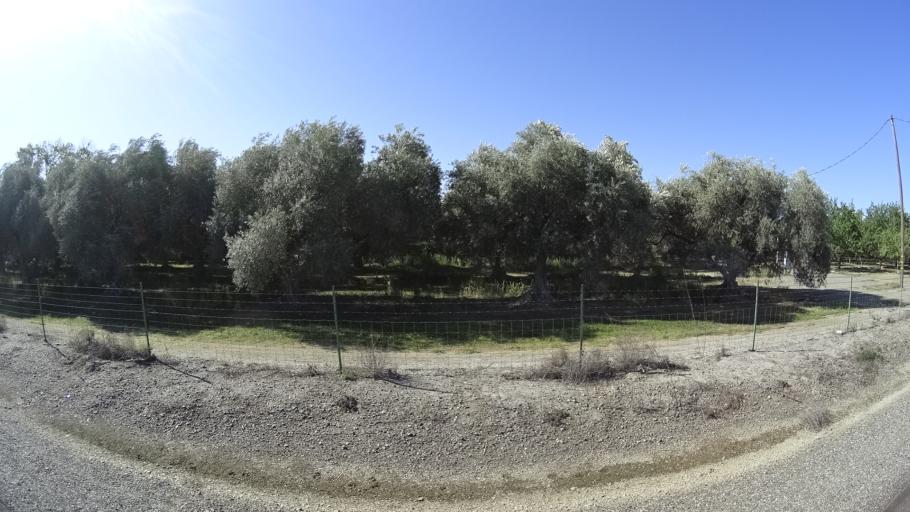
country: US
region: California
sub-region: Glenn County
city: Hamilton City
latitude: 39.7093
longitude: -122.0733
